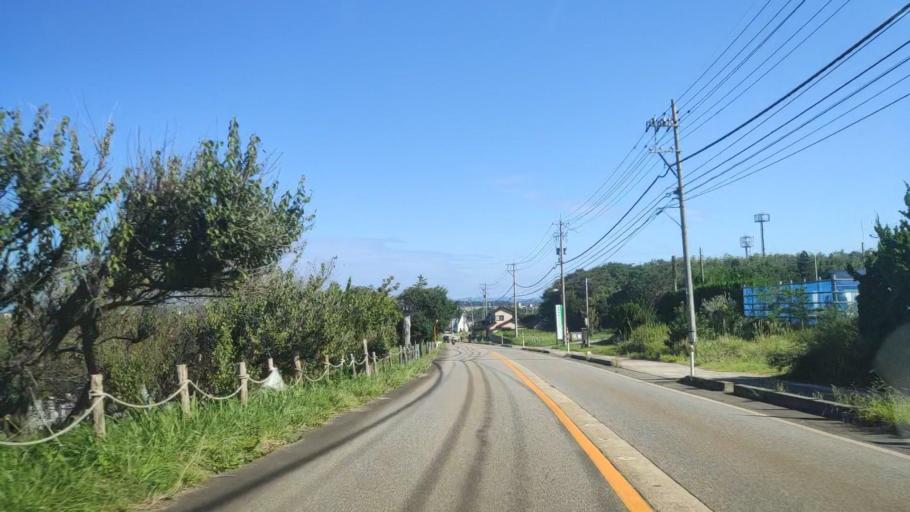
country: JP
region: Ishikawa
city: Hakui
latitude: 36.9918
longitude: 136.7767
